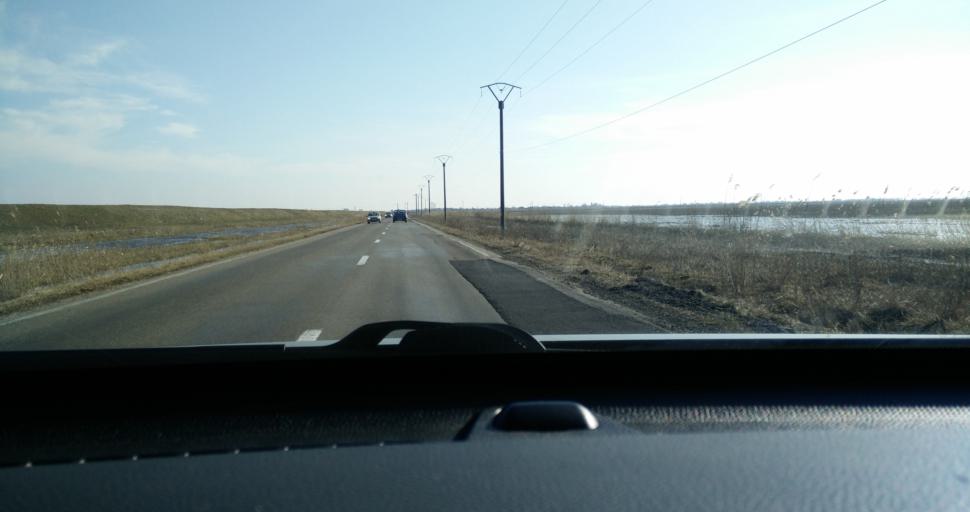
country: RO
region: Vrancea
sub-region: Comuna Nanesti
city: Nanesti
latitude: 45.5662
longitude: 27.4992
